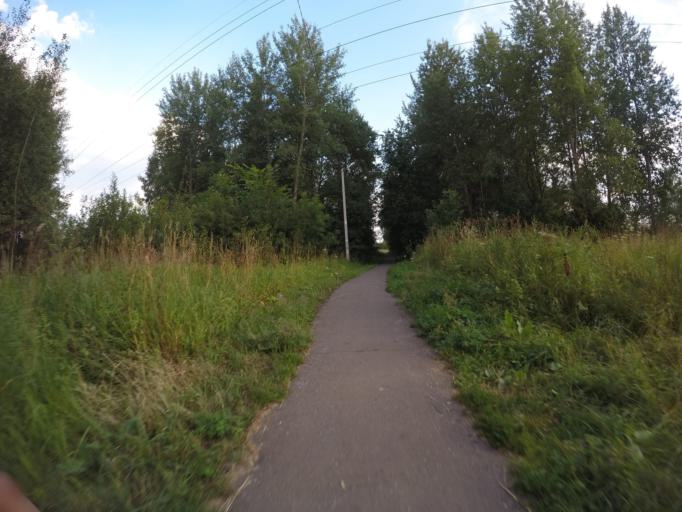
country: RU
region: Moskovskaya
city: Rechitsy
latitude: 55.6030
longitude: 38.5059
